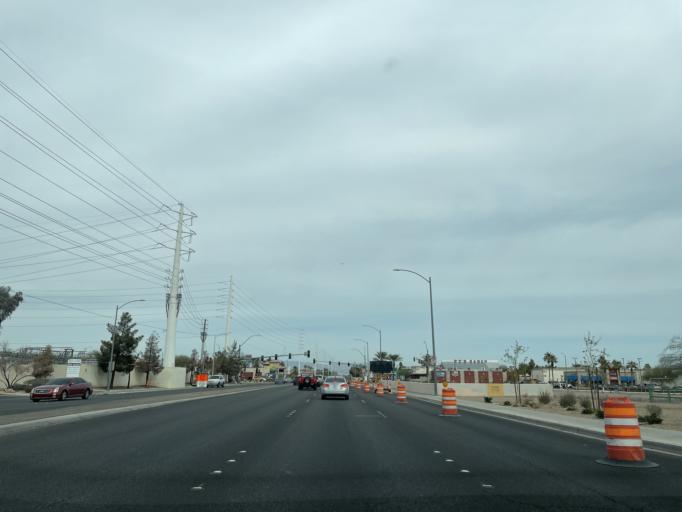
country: US
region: Nevada
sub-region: Clark County
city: Whitney
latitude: 36.0262
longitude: -115.1184
